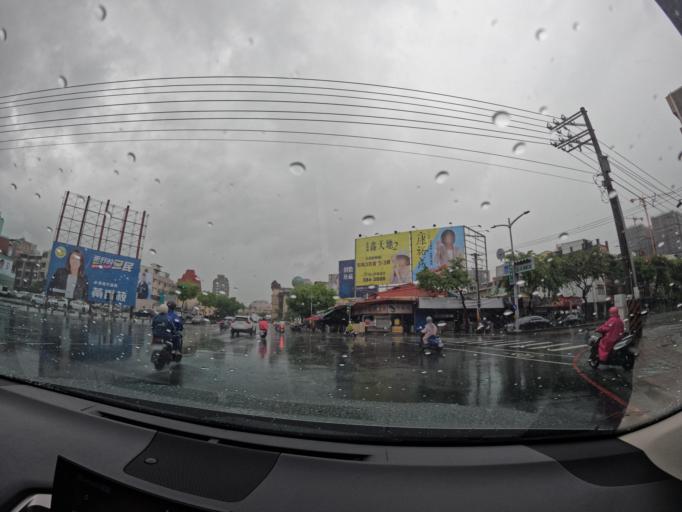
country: TW
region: Kaohsiung
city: Kaohsiung
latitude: 22.6604
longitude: 120.3221
